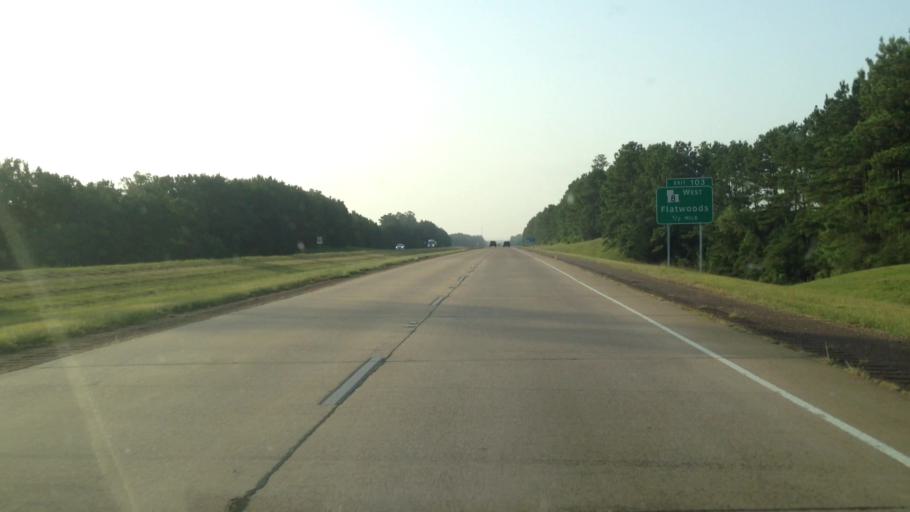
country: US
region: Louisiana
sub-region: Rapides Parish
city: Boyce
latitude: 31.4176
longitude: -92.7286
